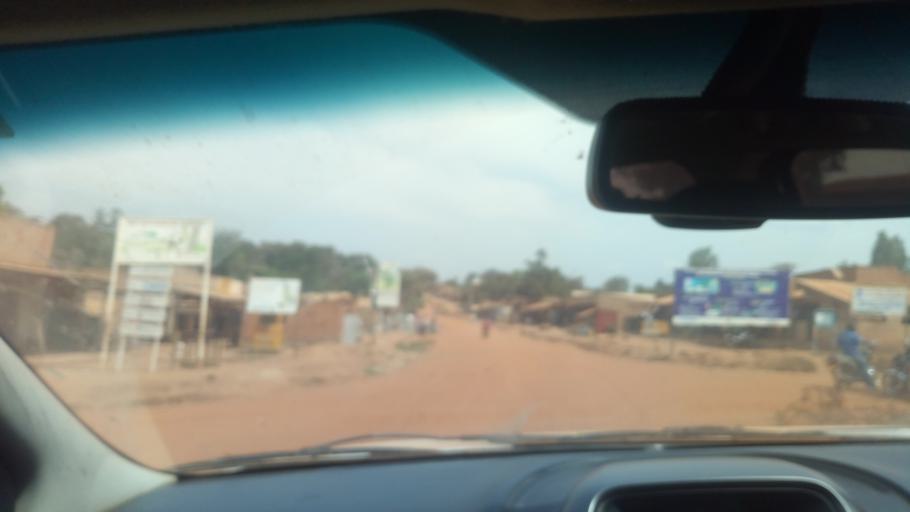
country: UG
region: Western Region
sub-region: Kiryandongo District
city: Kiryandongo
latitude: 1.9403
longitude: 32.1650
